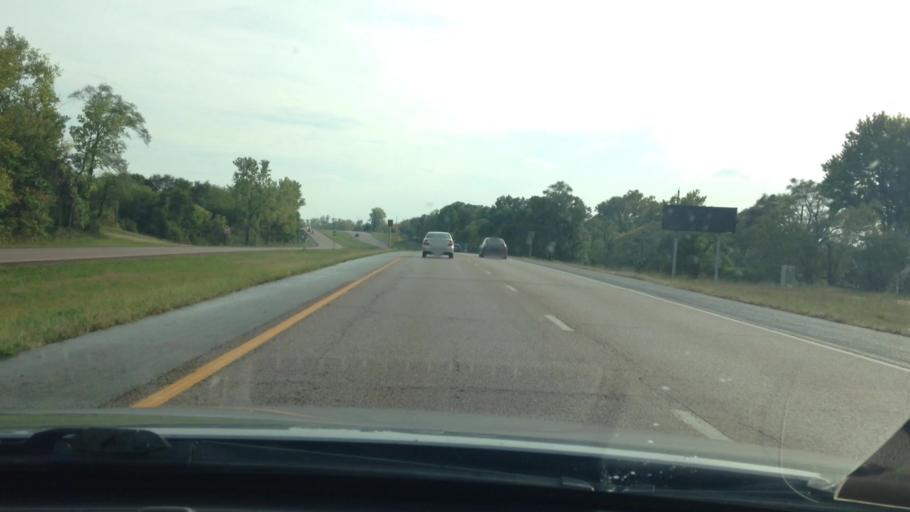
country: US
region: Kansas
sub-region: Leavenworth County
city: Basehor
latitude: 39.1355
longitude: -94.9006
